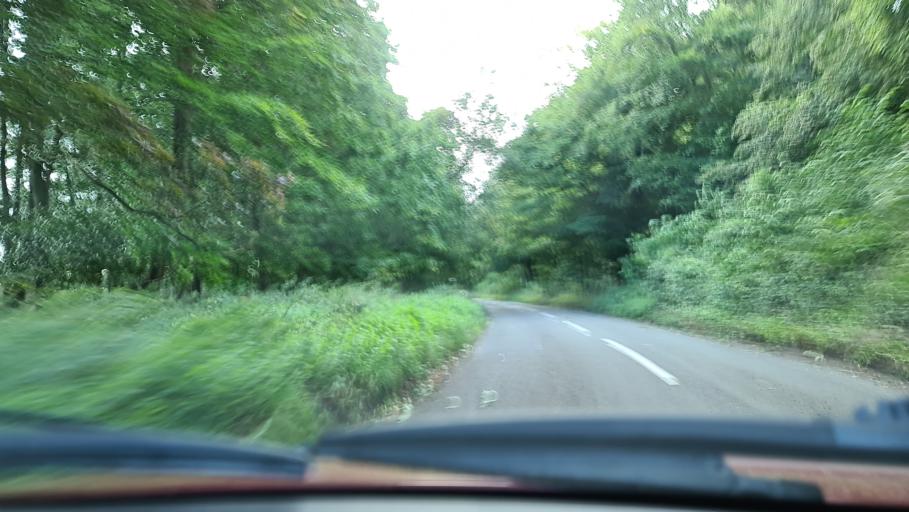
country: GB
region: England
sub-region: Buckinghamshire
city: Wendover
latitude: 51.7281
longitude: -0.7793
